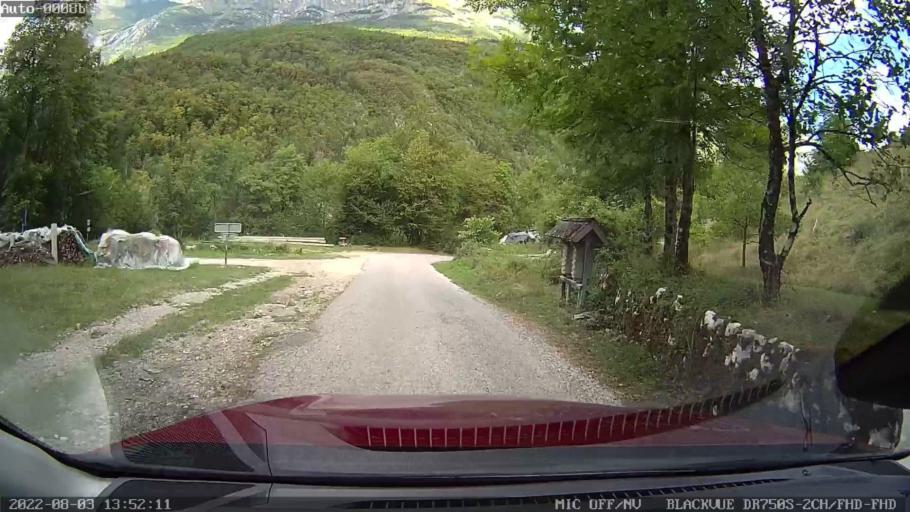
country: SI
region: Bovec
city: Bovec
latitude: 46.3401
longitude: 13.6848
